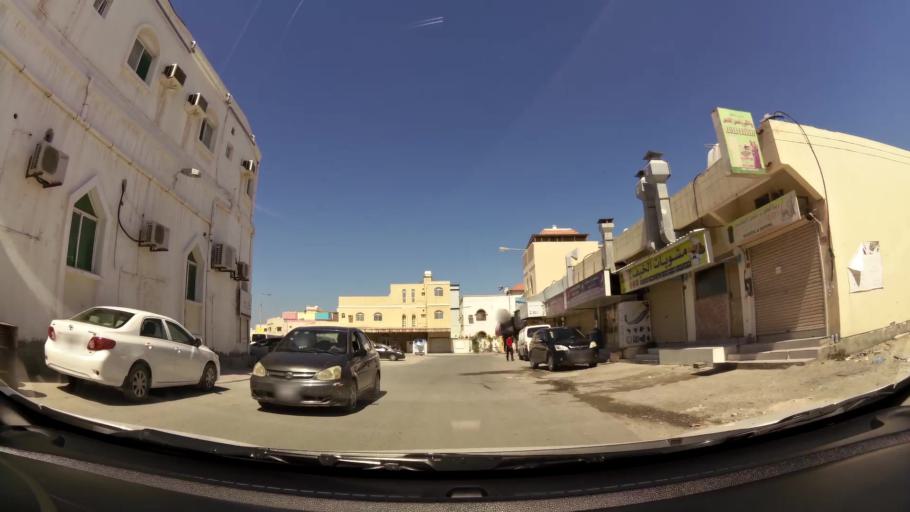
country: BH
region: Muharraq
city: Al Muharraq
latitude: 26.2862
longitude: 50.6269
